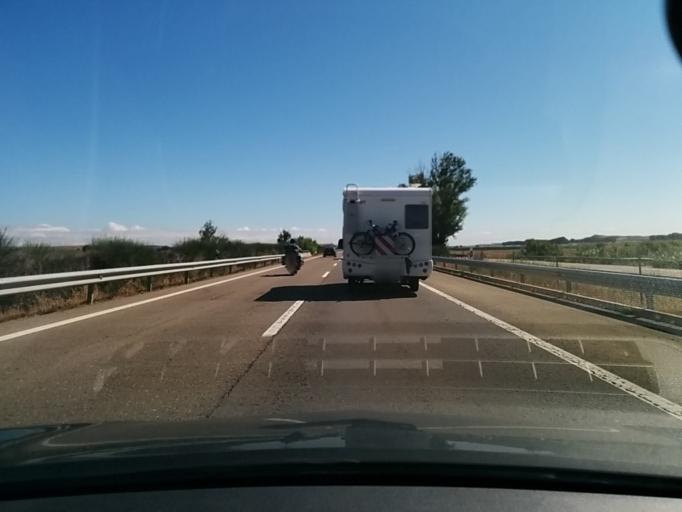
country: ES
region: Aragon
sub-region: Provincia de Huesca
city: Almudebar
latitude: 42.0035
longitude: -0.6408
